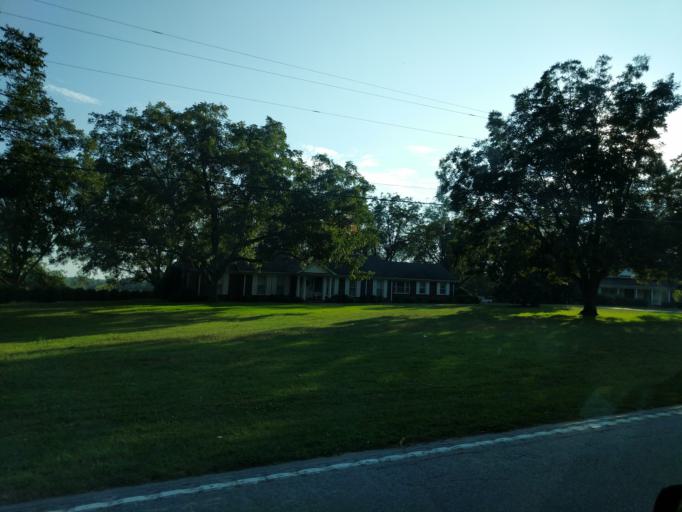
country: US
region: South Carolina
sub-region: Anderson County
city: Williamston
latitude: 34.6616
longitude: -82.5075
